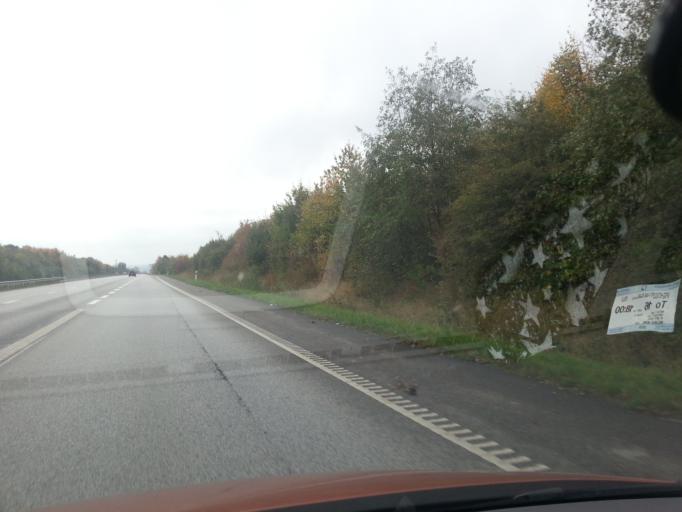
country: SE
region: Skane
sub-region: Lunds Kommun
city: Lund
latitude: 55.7152
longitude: 13.2224
